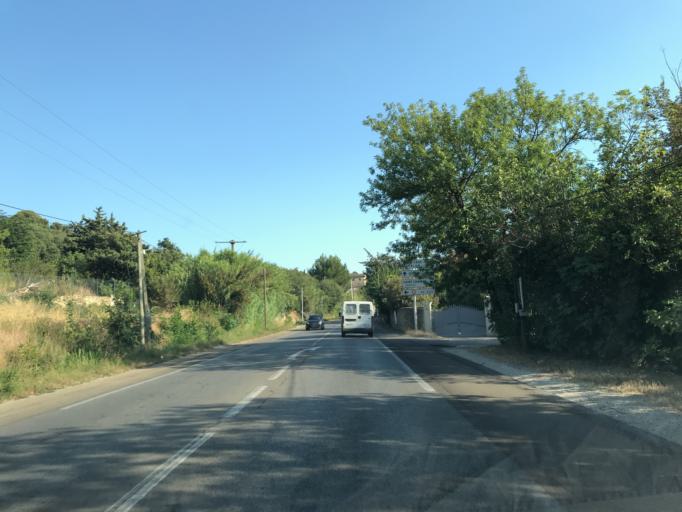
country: FR
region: Provence-Alpes-Cote d'Azur
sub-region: Departement des Bouches-du-Rhone
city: Saint-Chamas
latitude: 43.5597
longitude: 5.0310
